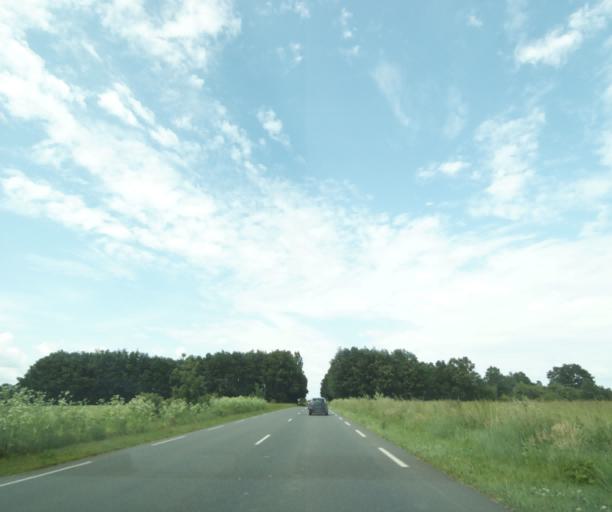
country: FR
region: Pays de la Loire
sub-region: Departement de Maine-et-Loire
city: Montreuil-Bellay
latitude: 47.1696
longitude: -0.1391
